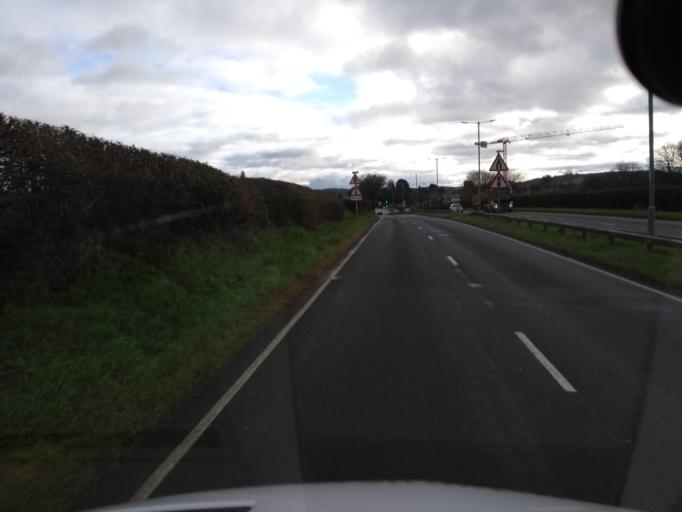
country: GB
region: England
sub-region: Dorset
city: Sherborne
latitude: 50.9484
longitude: -2.5352
